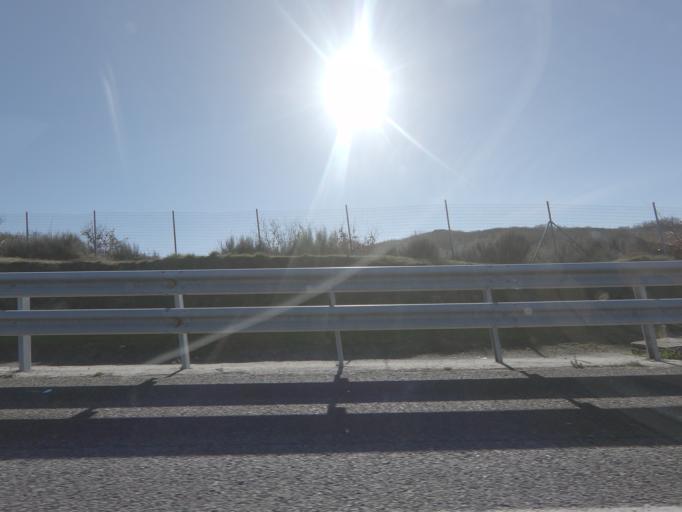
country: ES
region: Galicia
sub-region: Provincia de Ourense
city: Cualedro
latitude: 42.0102
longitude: -7.5779
